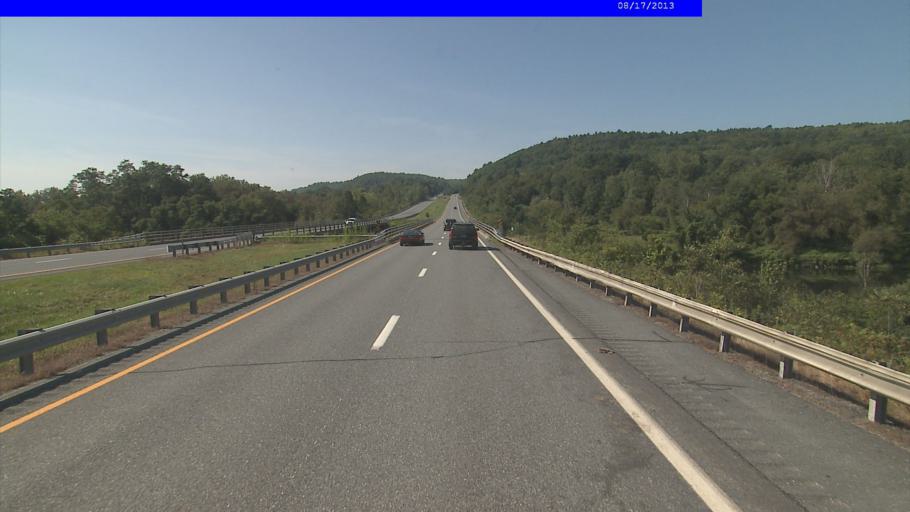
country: US
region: New Hampshire
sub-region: Sullivan County
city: Charlestown
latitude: 43.2621
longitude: -72.4354
